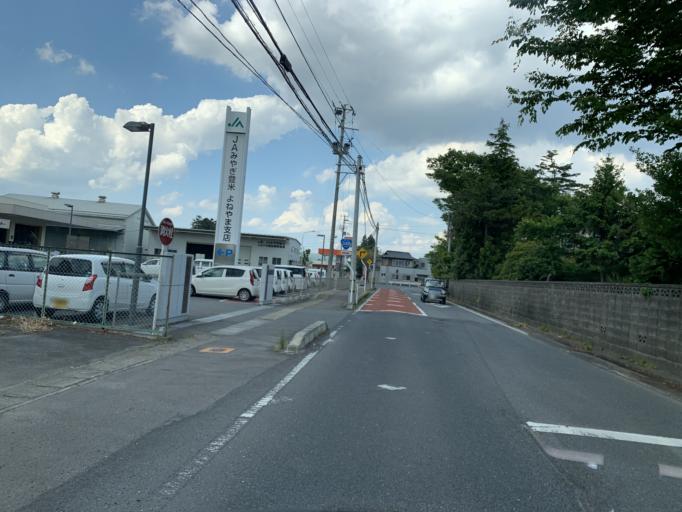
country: JP
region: Miyagi
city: Wakuya
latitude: 38.6289
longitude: 141.1909
